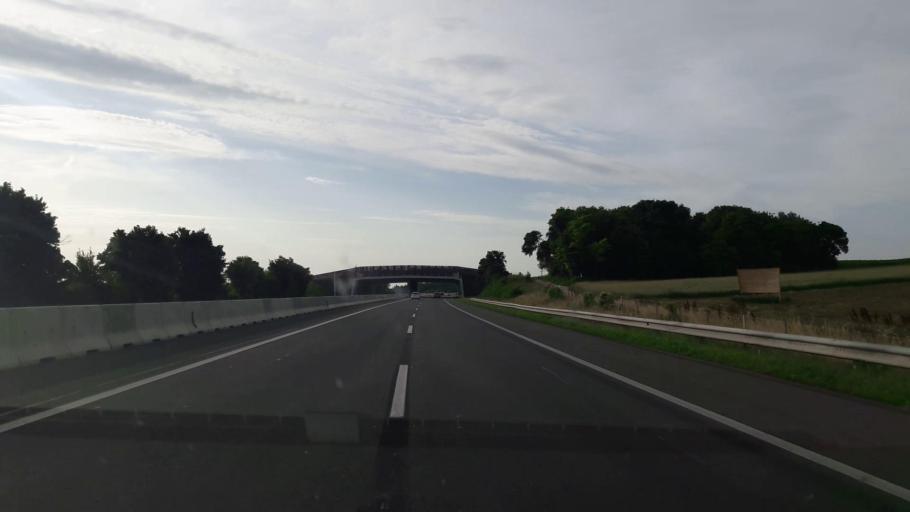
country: AT
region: Burgenland
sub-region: Eisenstadt-Umgebung
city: Steinbrunn
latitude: 47.8467
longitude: 16.4318
